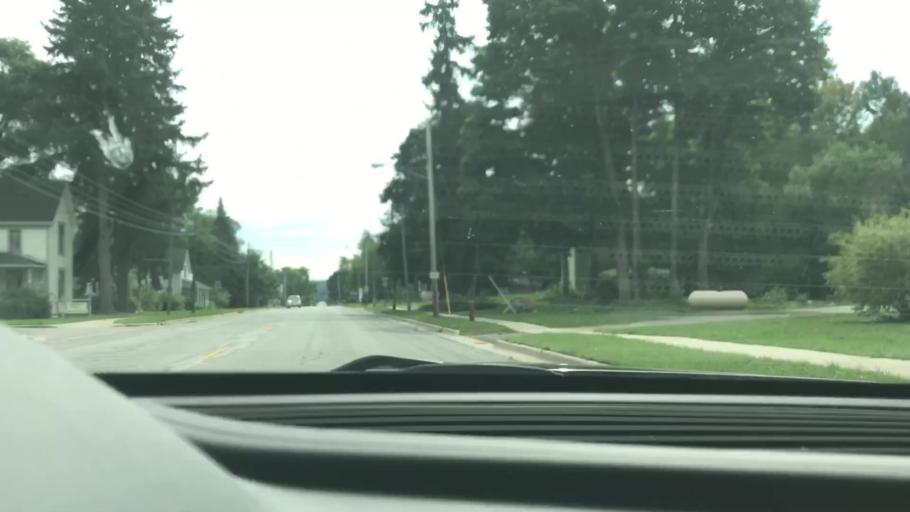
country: US
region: Michigan
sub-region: Antrim County
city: Bellaire
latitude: 45.0683
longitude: -85.2642
